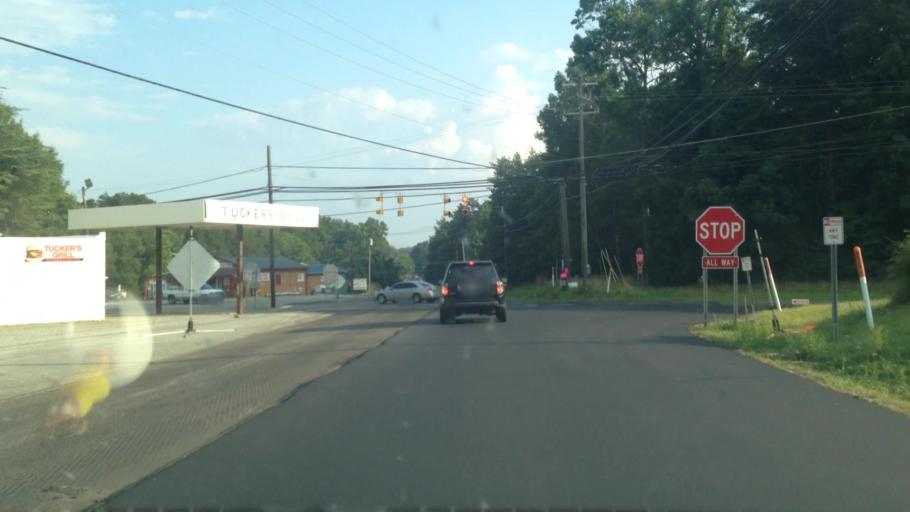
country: US
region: North Carolina
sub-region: Davidson County
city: Wallburg
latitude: 36.0200
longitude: -80.0599
